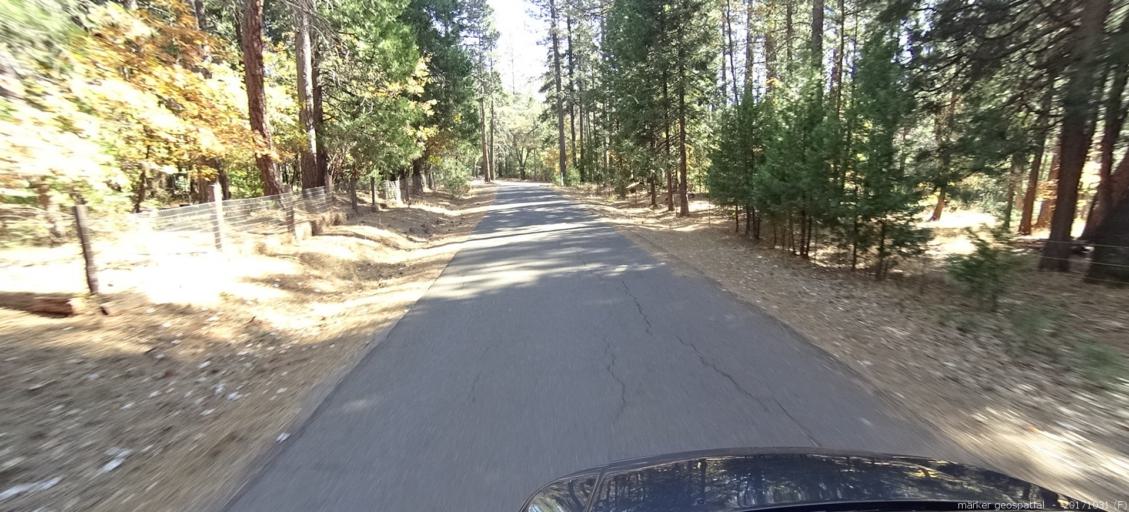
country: US
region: California
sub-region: Shasta County
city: Shingletown
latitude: 40.5161
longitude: -121.9368
